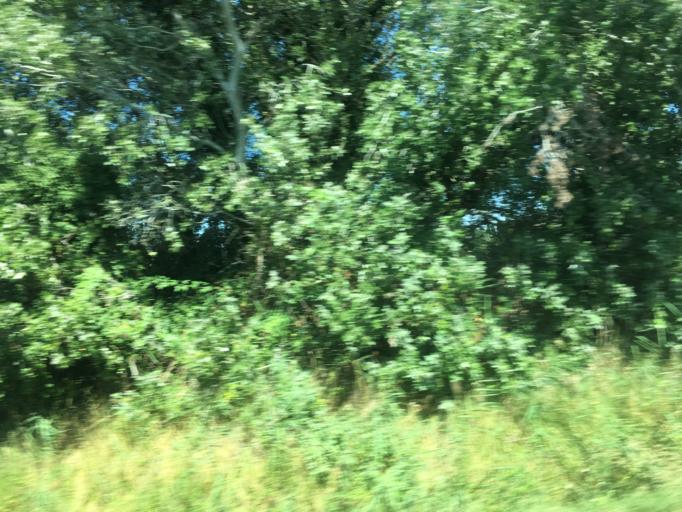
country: FR
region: Languedoc-Roussillon
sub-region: Departement du Gard
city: Saint-Gilles
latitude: 43.5856
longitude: 4.4696
